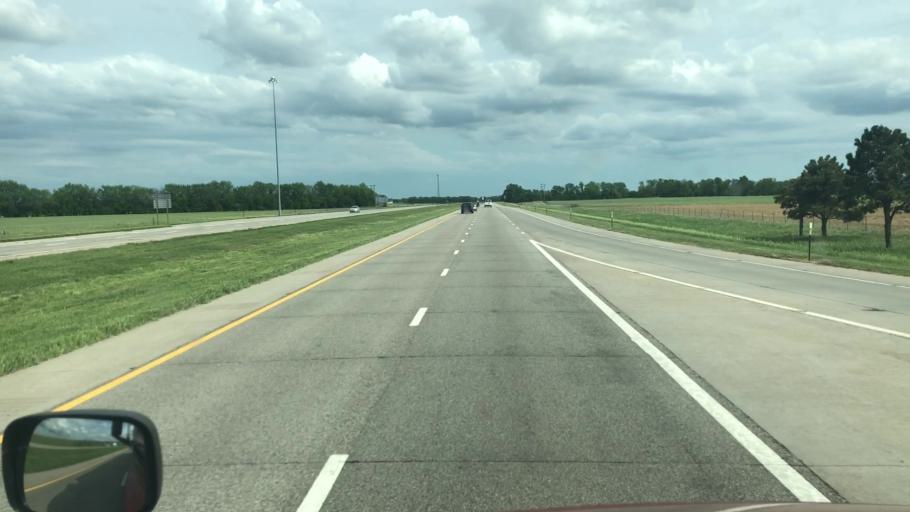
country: US
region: Kansas
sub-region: McPherson County
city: Moundridge
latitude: 38.2014
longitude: -97.4860
